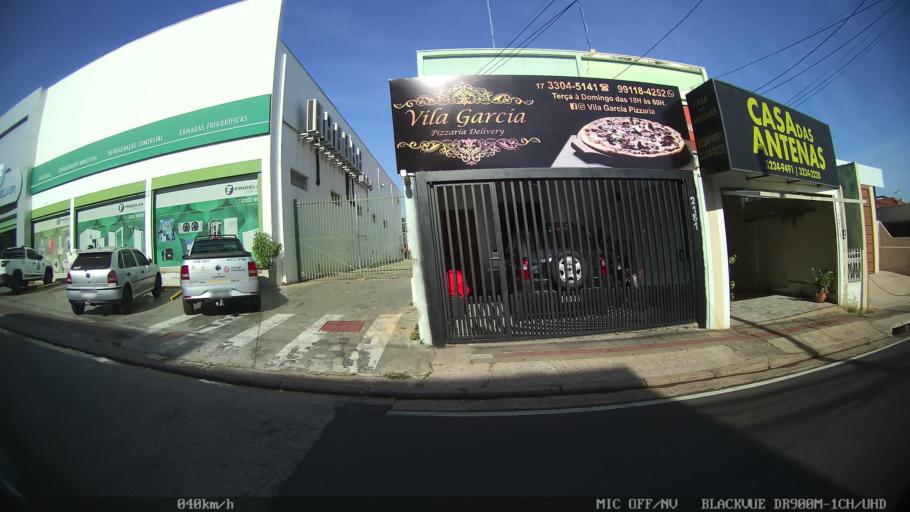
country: BR
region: Sao Paulo
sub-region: Sao Jose Do Rio Preto
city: Sao Jose do Rio Preto
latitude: -20.8065
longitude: -49.3755
